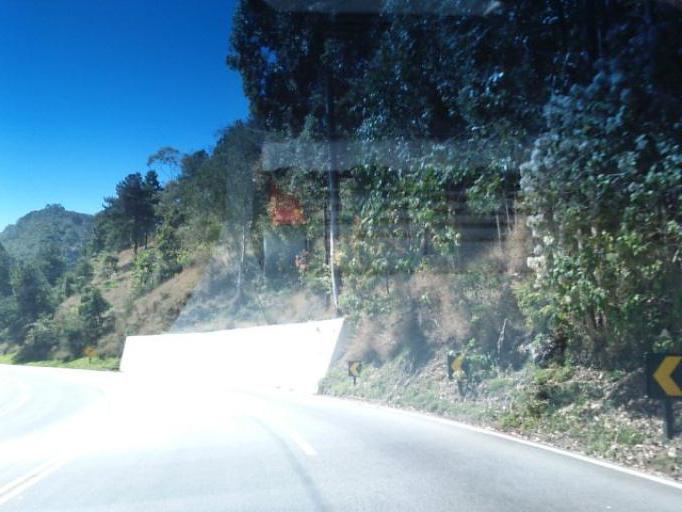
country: BR
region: Sao Paulo
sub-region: Campos Do Jordao
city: Campos do Jordao
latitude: -22.7858
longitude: -45.6154
